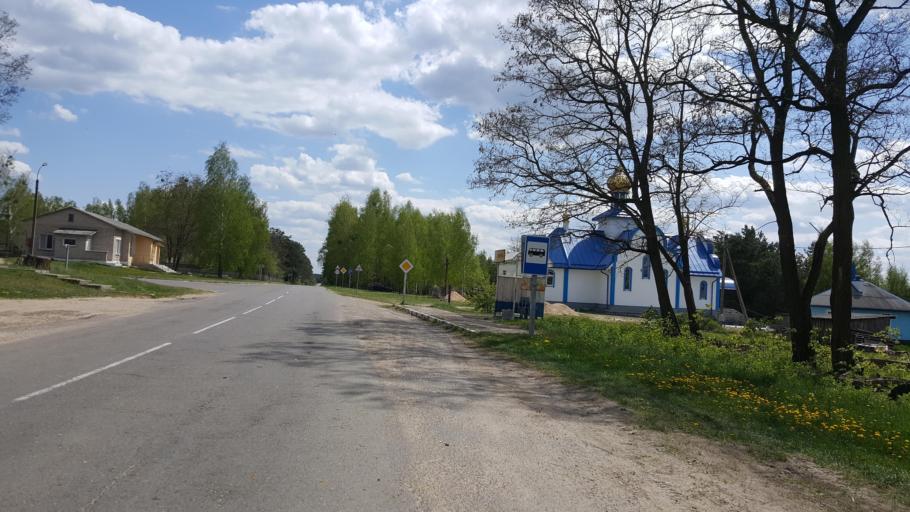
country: BY
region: Brest
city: Zhabinka
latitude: 52.4216
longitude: 24.1671
